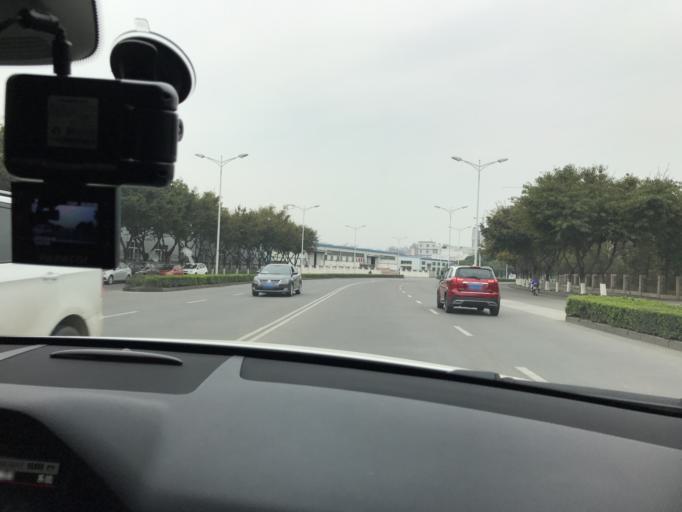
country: CN
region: Sichuan
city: Mianyang
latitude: 31.4587
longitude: 104.6762
